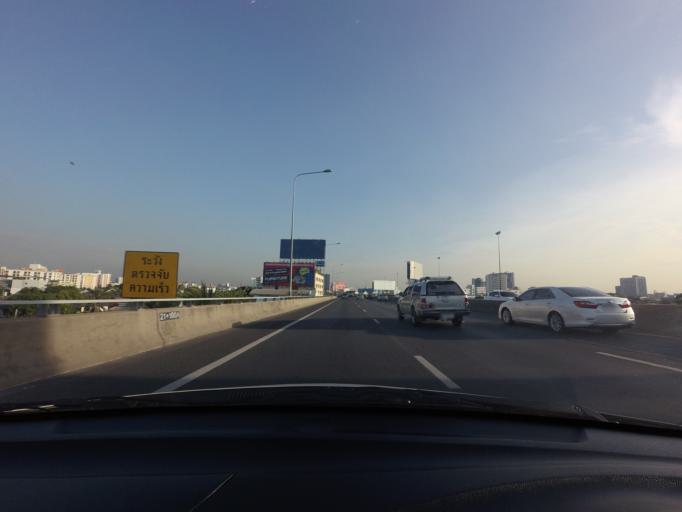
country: TH
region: Nonthaburi
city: Mueang Nonthaburi
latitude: 13.8663
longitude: 100.5337
